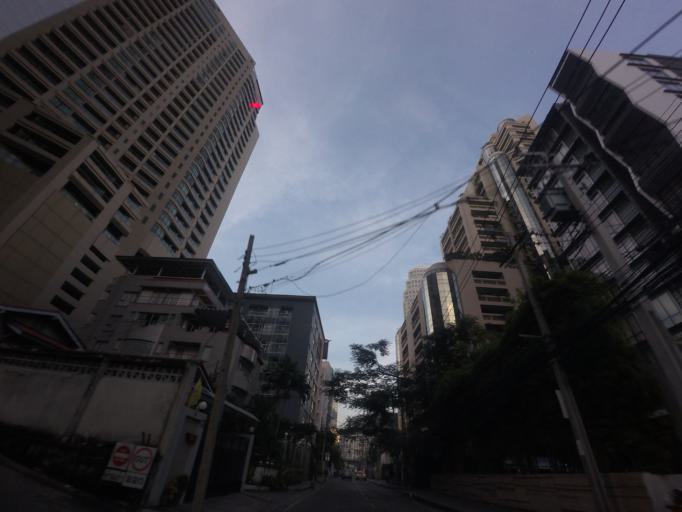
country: TH
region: Bangkok
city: Khlong Toei
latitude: 13.7332
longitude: 100.5610
